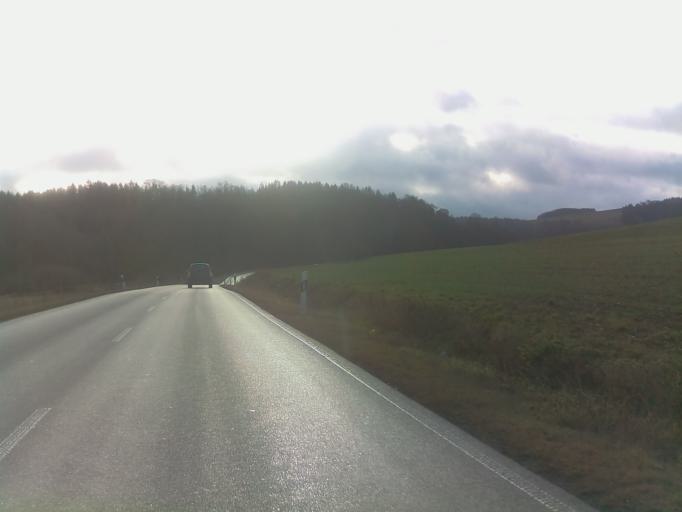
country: DE
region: Thuringia
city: Allendorf
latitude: 50.6654
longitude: 11.1514
